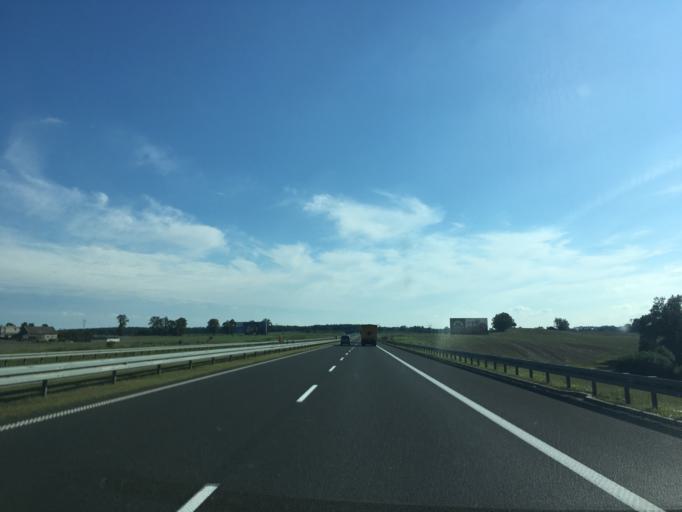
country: PL
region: Kujawsko-Pomorskie
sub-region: Powiat swiecki
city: Warlubie
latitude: 53.5653
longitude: 18.6082
